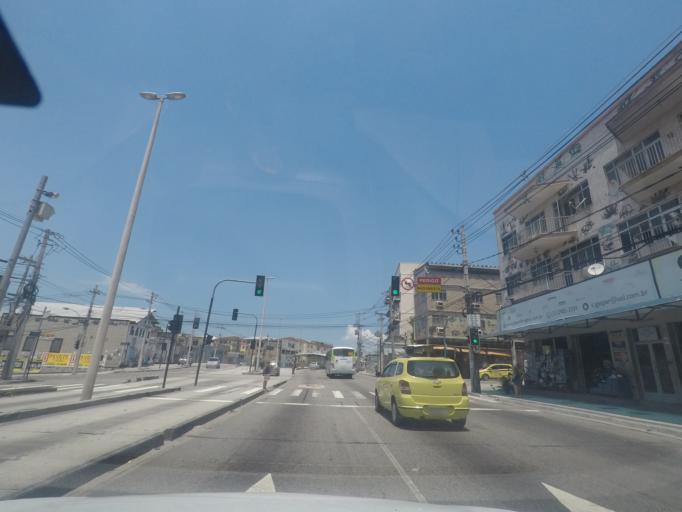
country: BR
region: Rio de Janeiro
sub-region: Duque De Caxias
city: Duque de Caxias
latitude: -22.8379
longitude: -43.2911
